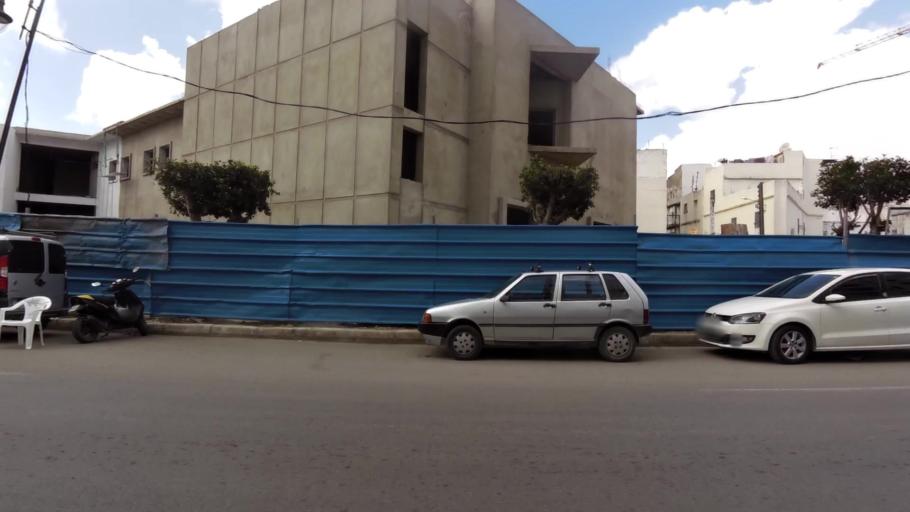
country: MA
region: Tanger-Tetouan
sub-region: Tanger-Assilah
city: Tangier
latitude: 35.7549
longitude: -5.8107
